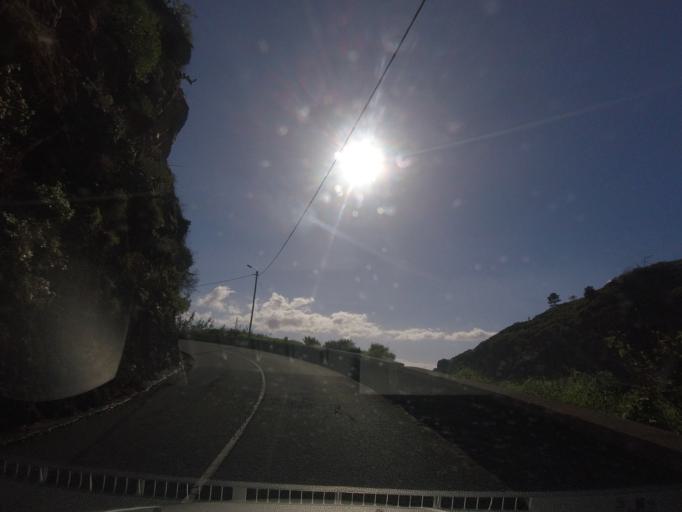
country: PT
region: Madeira
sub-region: Calheta
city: Estreito da Calheta
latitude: 32.7355
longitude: -17.1993
